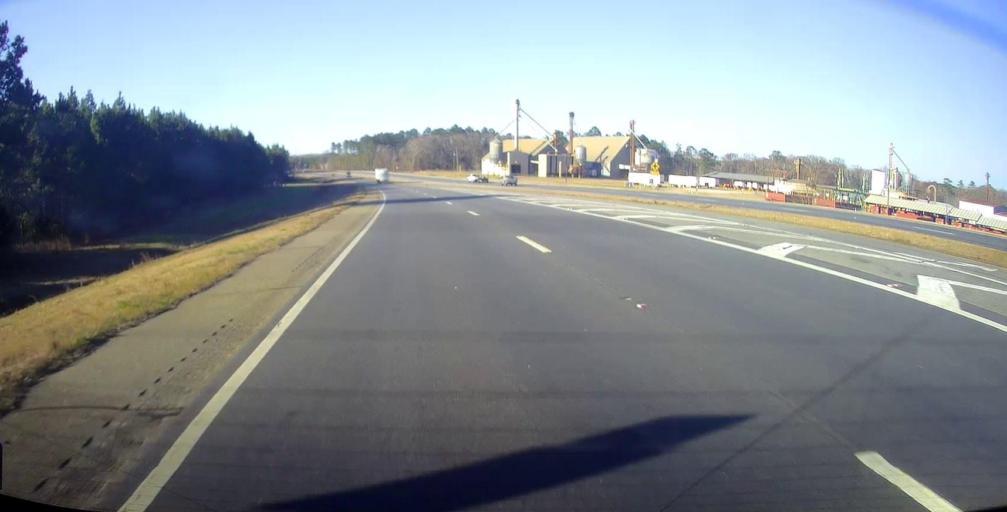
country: US
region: Georgia
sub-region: Sumter County
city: Americus
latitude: 31.9129
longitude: -84.2596
